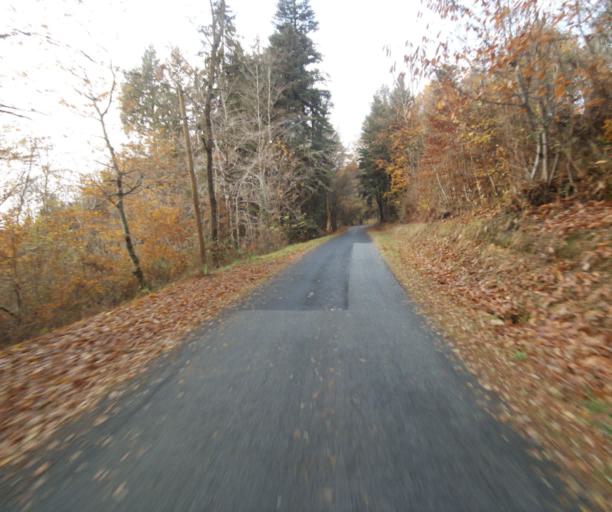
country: FR
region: Limousin
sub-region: Departement de la Correze
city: Cornil
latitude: 45.2219
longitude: 1.6919
